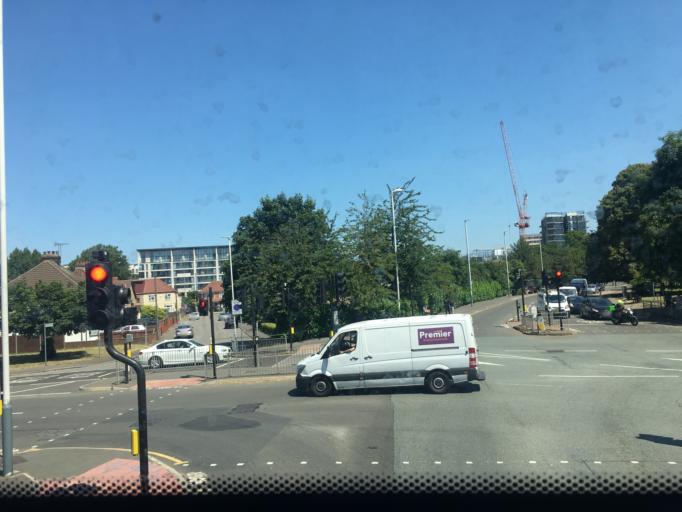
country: GB
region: England
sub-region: Greater London
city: Hayes
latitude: 51.5011
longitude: -0.4243
